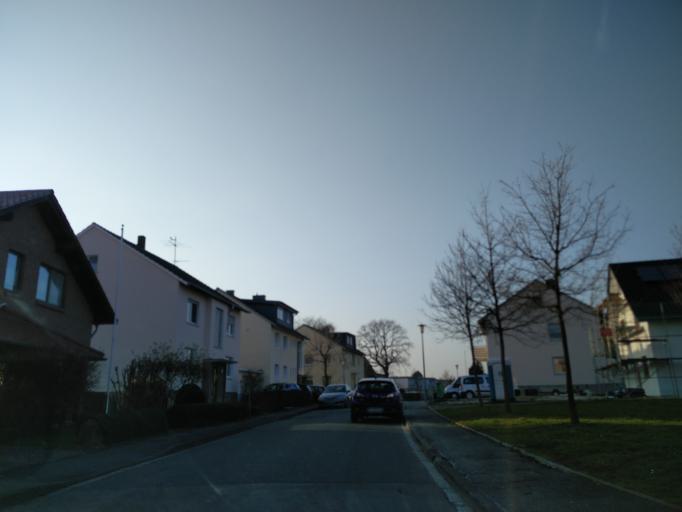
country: DE
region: North Rhine-Westphalia
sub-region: Regierungsbezirk Detmold
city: Paderborn
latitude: 51.6901
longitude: 8.6897
